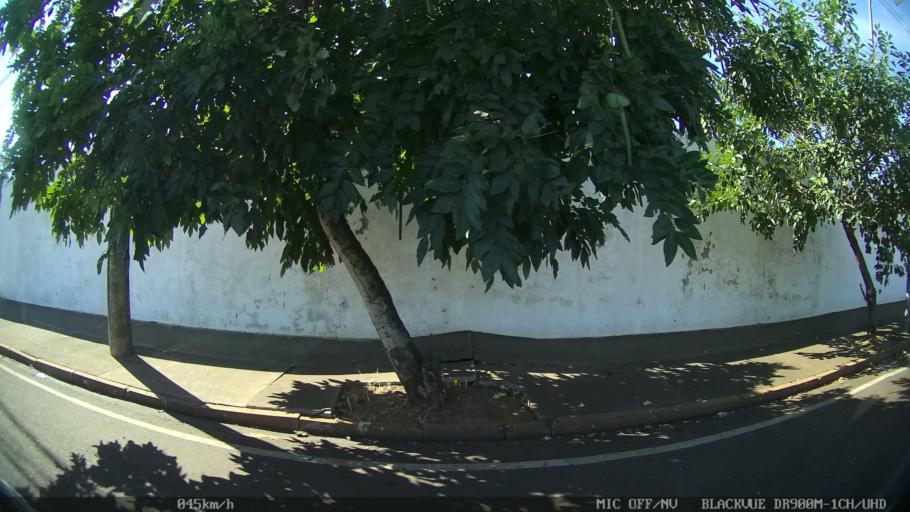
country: BR
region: Sao Paulo
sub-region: Sao Jose Do Rio Preto
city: Sao Jose do Rio Preto
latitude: -20.8108
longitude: -49.4114
